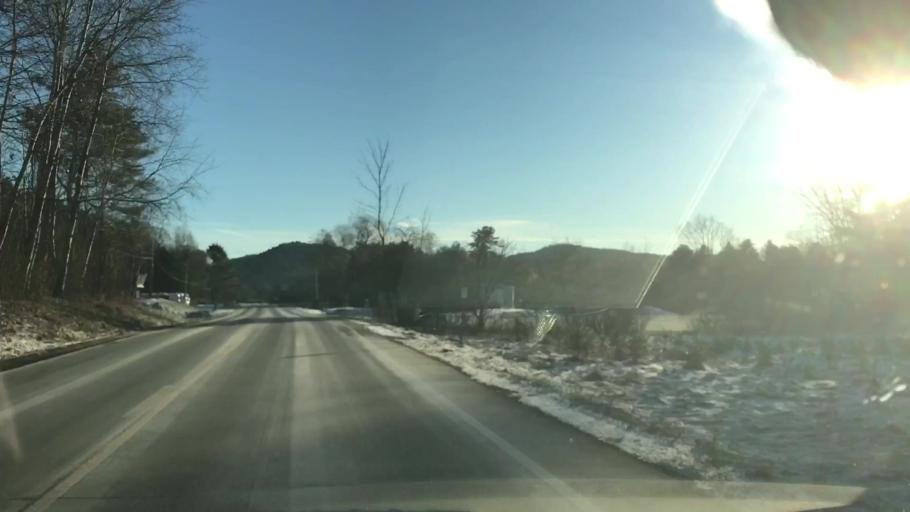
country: US
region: New Hampshire
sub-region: Grafton County
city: Lyme Town Offices
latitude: 43.8562
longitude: -72.1555
